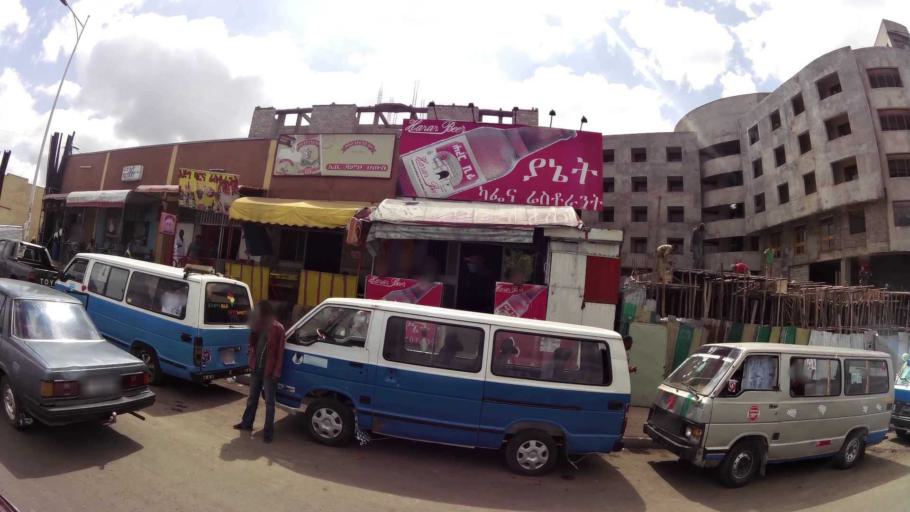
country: ET
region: Adis Abeba
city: Addis Ababa
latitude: 8.9525
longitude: 38.7613
